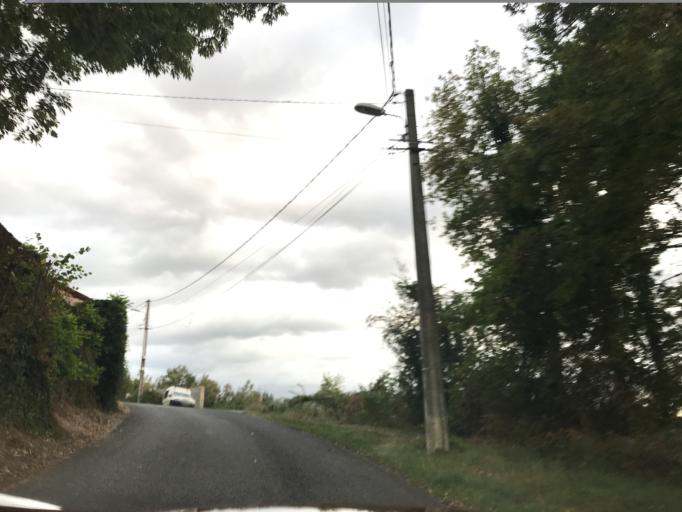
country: FR
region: Auvergne
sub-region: Departement du Puy-de-Dome
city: Thiers
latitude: 45.8459
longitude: 3.5386
